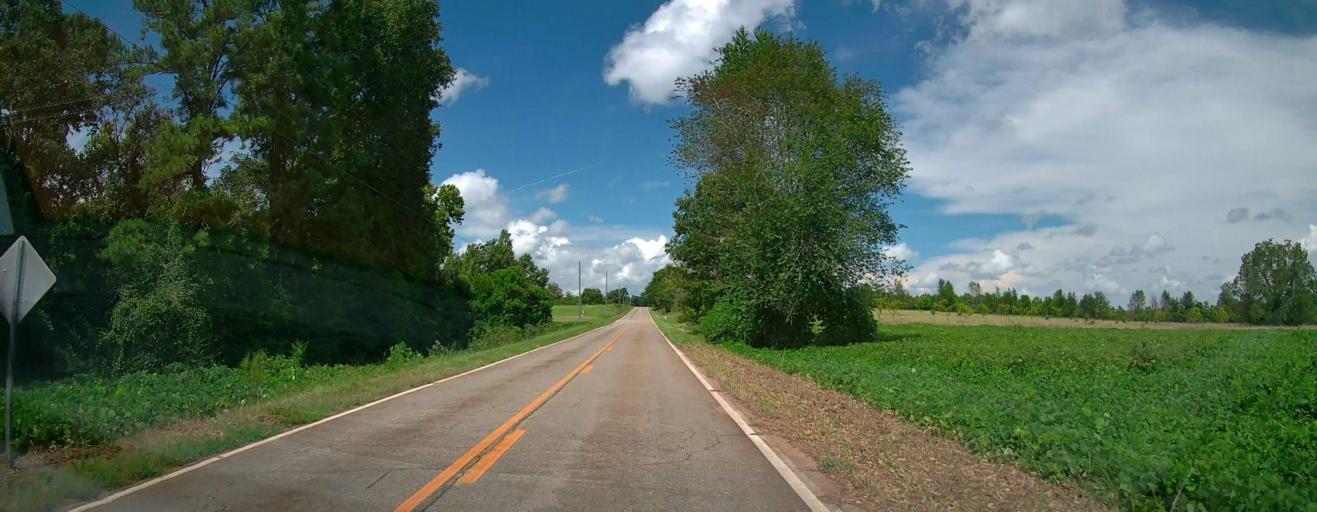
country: US
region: Georgia
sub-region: Peach County
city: Fort Valley
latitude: 32.5263
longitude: -83.8025
